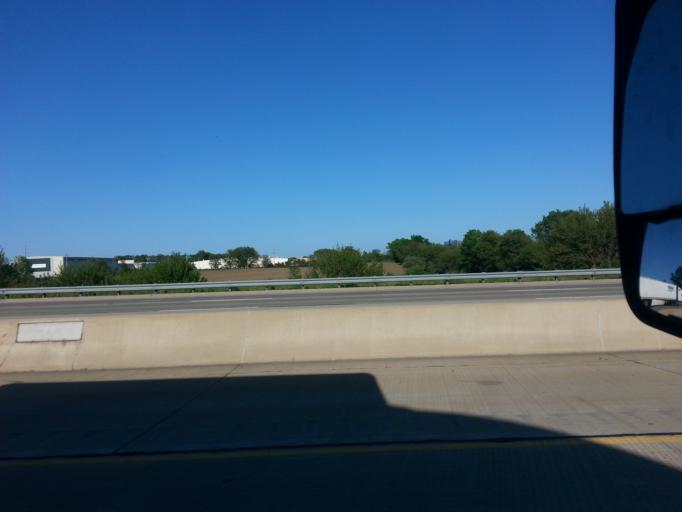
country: US
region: Illinois
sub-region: McLean County
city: Bloomington
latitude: 40.4992
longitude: -89.0288
